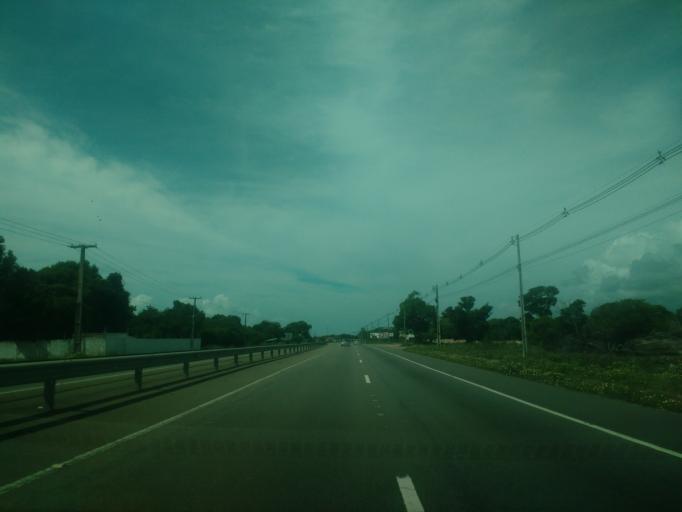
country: BR
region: Alagoas
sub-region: Marechal Deodoro
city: Marechal Deodoro
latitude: -9.7539
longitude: -35.8413
